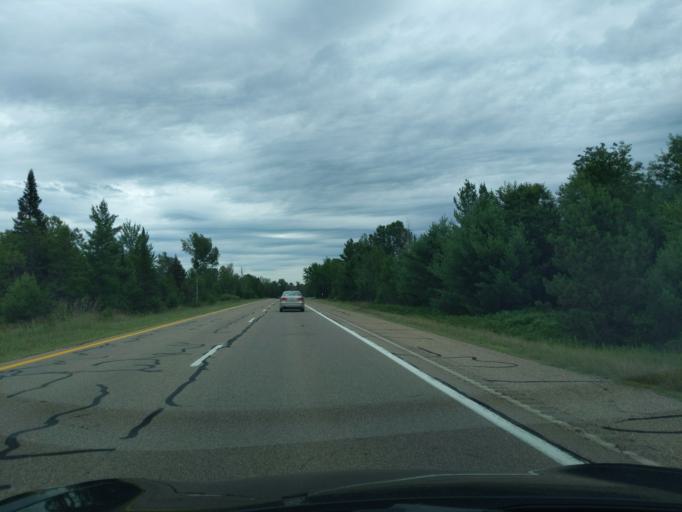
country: US
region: Michigan
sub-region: Roscommon County
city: Houghton Lake
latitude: 44.3021
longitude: -84.8030
